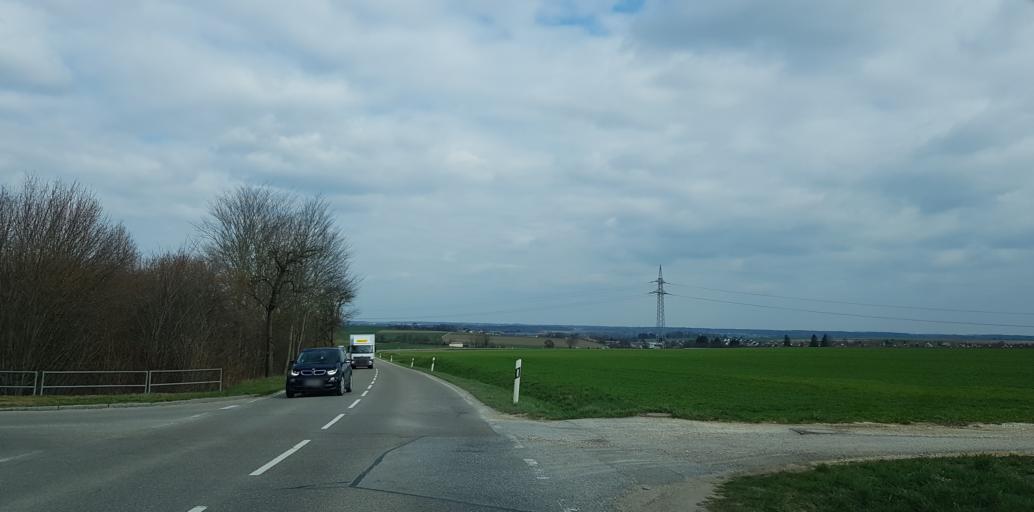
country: DE
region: Baden-Wuerttemberg
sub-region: Tuebingen Region
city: Erbach
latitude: 48.3606
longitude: 9.8819
